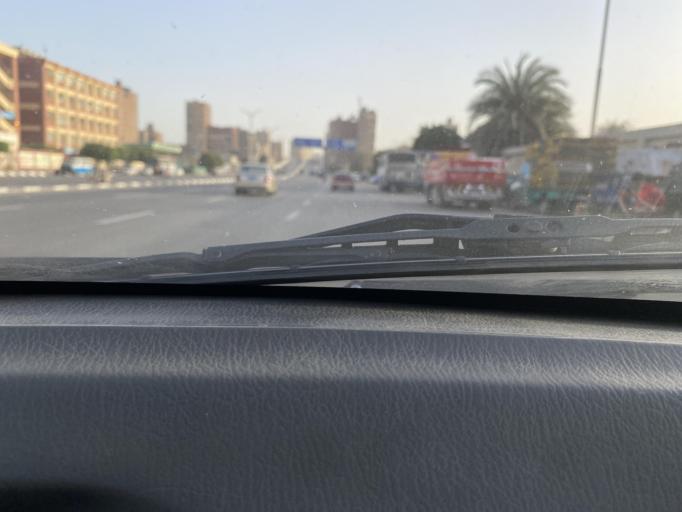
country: EG
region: Muhafazat al Qahirah
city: Cairo
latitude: 30.1168
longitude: 31.2964
